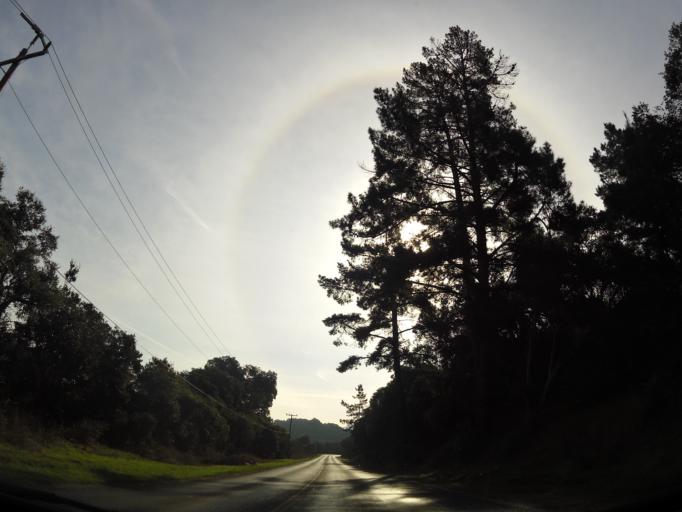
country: US
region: California
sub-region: Monterey County
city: Prunedale
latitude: 36.7934
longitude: -121.6145
